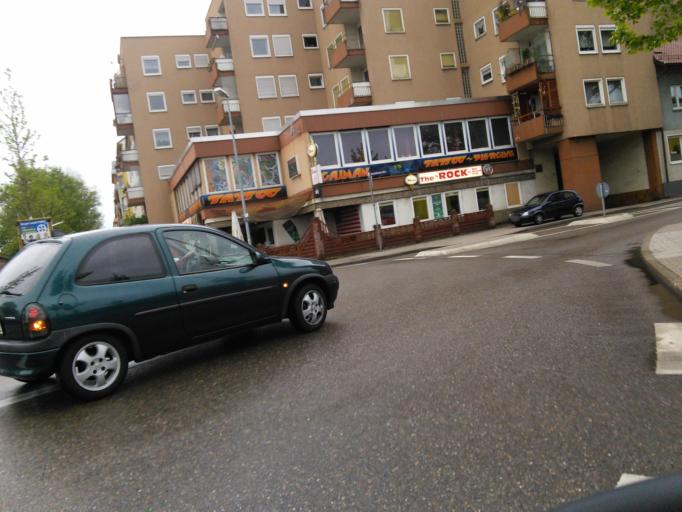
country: DE
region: Baden-Wuerttemberg
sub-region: Karlsruhe Region
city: Pforzheim
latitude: 48.8960
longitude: 8.7108
